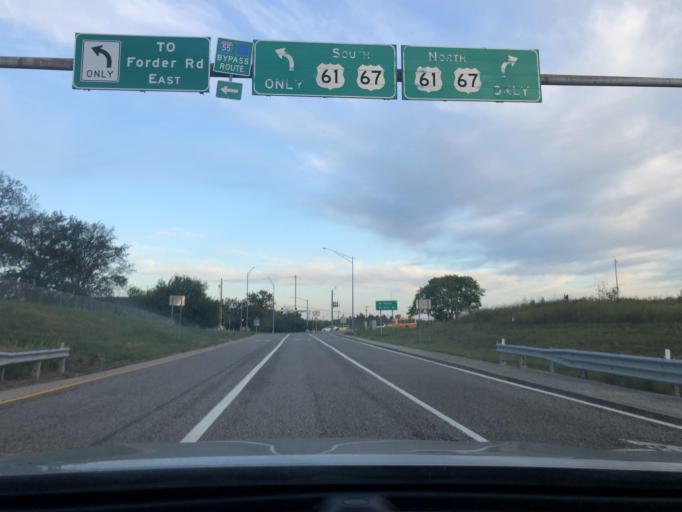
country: US
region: Missouri
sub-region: Saint Louis County
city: Mehlville
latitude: 38.5014
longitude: -90.3297
